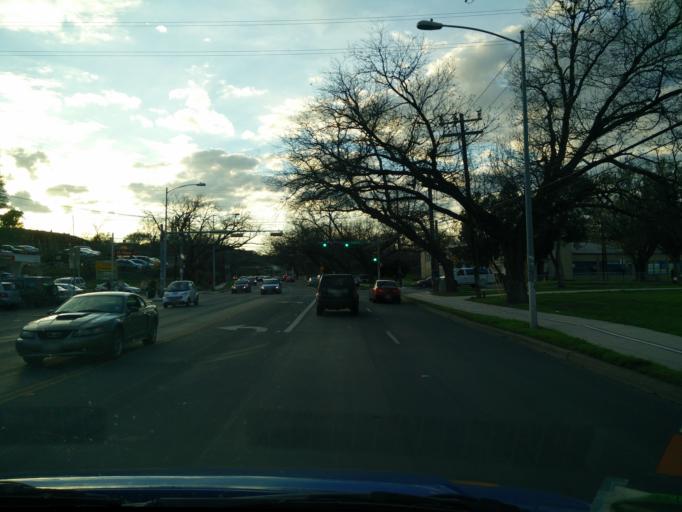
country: US
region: Texas
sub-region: Travis County
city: Austin
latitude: 30.2602
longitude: -97.7551
